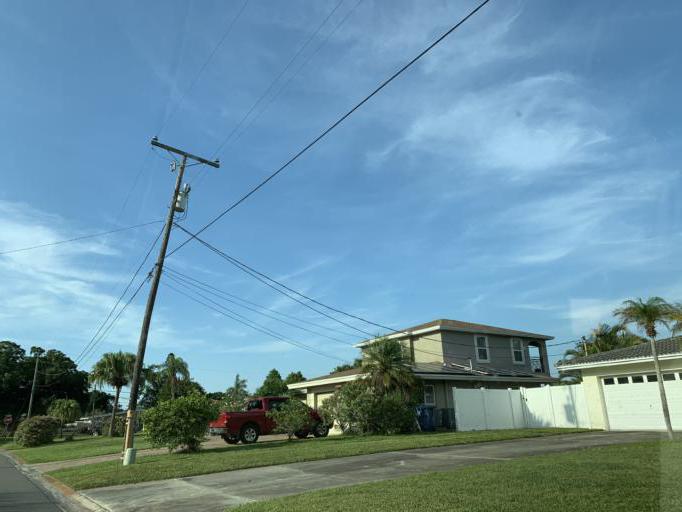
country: US
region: Florida
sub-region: Pinellas County
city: Lealman
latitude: 27.8060
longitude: -82.6208
